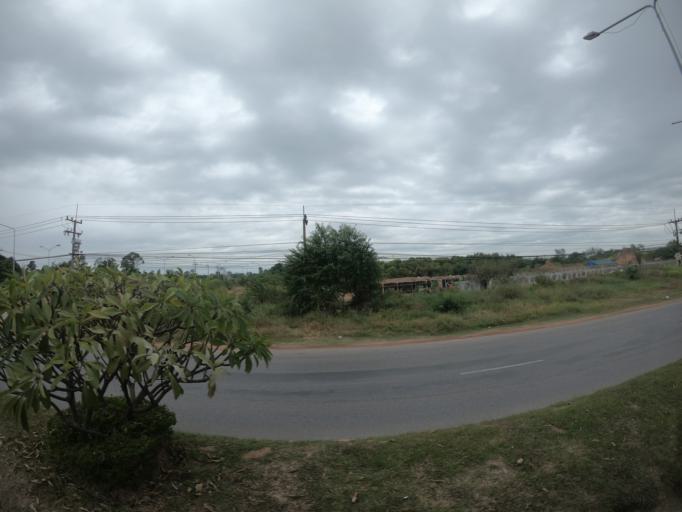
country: TH
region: Maha Sarakham
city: Maha Sarakham
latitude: 16.1700
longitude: 103.2915
